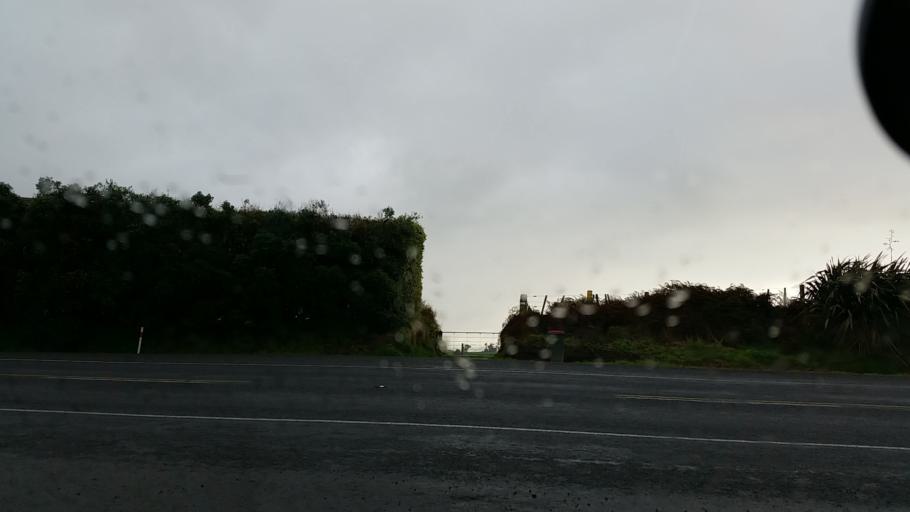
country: NZ
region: Taranaki
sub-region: South Taranaki District
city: Patea
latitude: -39.7637
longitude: 174.6425
